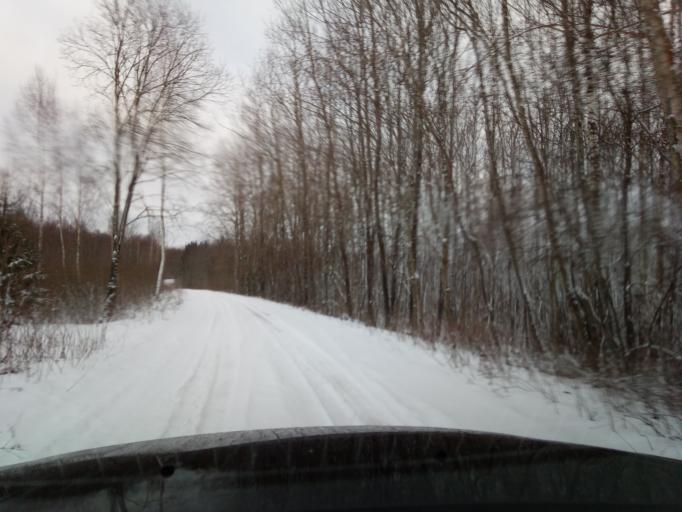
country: LT
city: Zarasai
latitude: 55.7323
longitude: 25.9435
